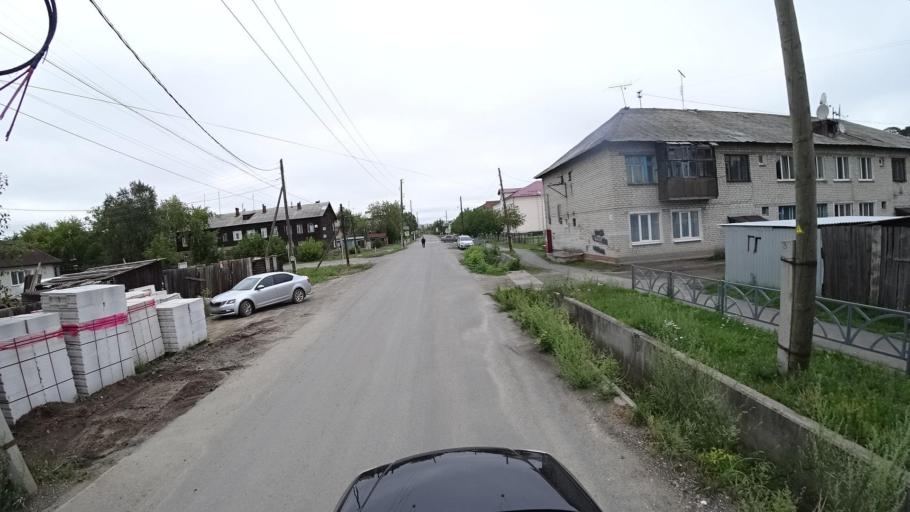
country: RU
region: Sverdlovsk
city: Kamyshlov
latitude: 56.8401
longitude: 62.7387
